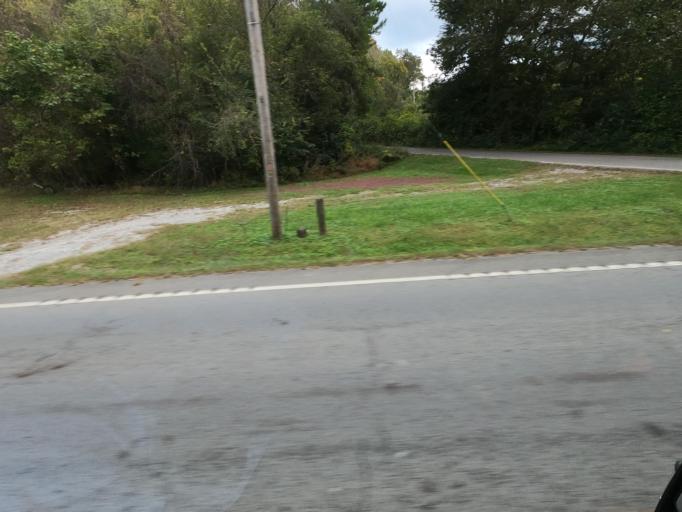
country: US
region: Tennessee
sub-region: Cheatham County
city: Pegram
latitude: 36.0981
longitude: -87.0471
